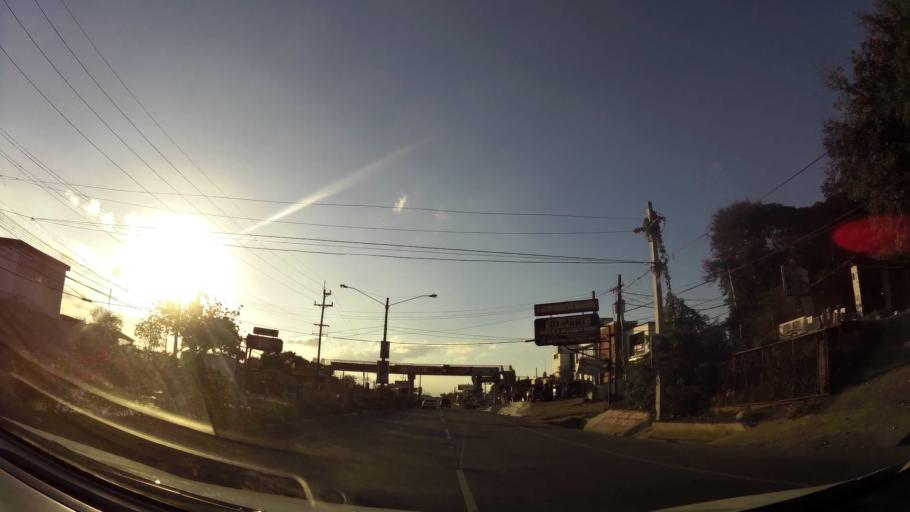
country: DO
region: Santiago
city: Palmar Arriba
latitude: 19.4983
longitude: -70.7390
